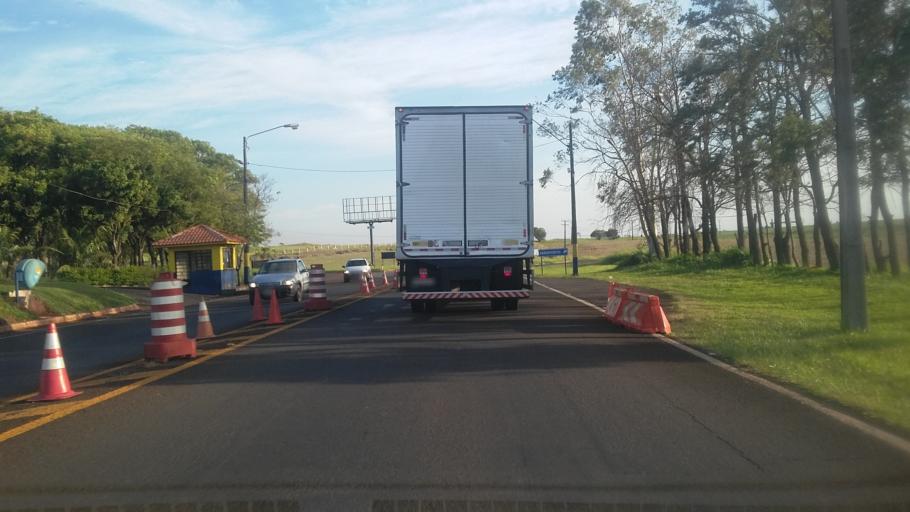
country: BR
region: Parana
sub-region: Bandeirantes
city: Bandeirantes
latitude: -23.1604
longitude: -50.6082
